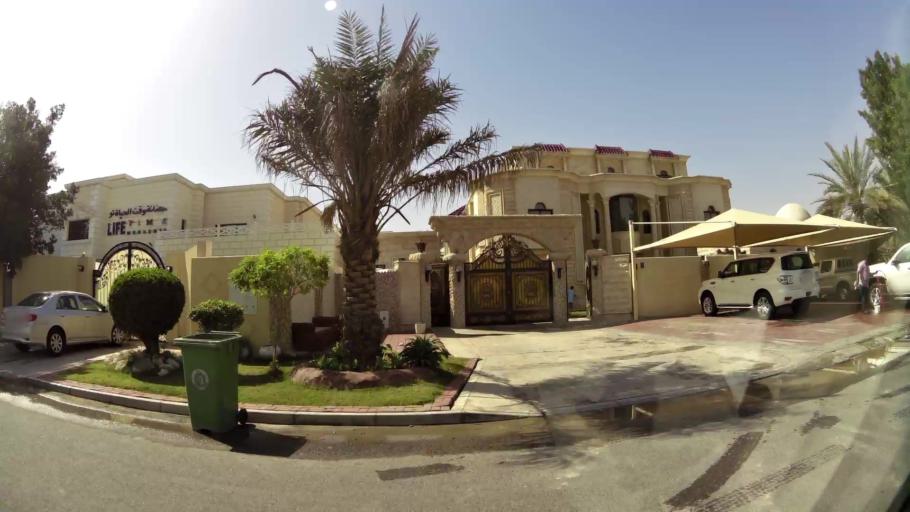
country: QA
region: Baladiyat ad Dawhah
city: Doha
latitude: 25.3530
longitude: 51.5153
